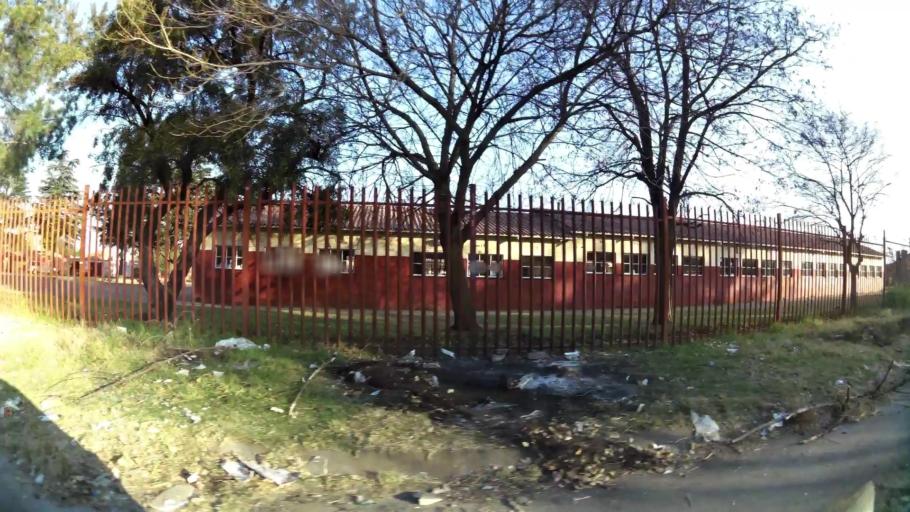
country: ZA
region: Gauteng
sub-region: City of Johannesburg Metropolitan Municipality
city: Soweto
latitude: -26.2544
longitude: 27.8793
